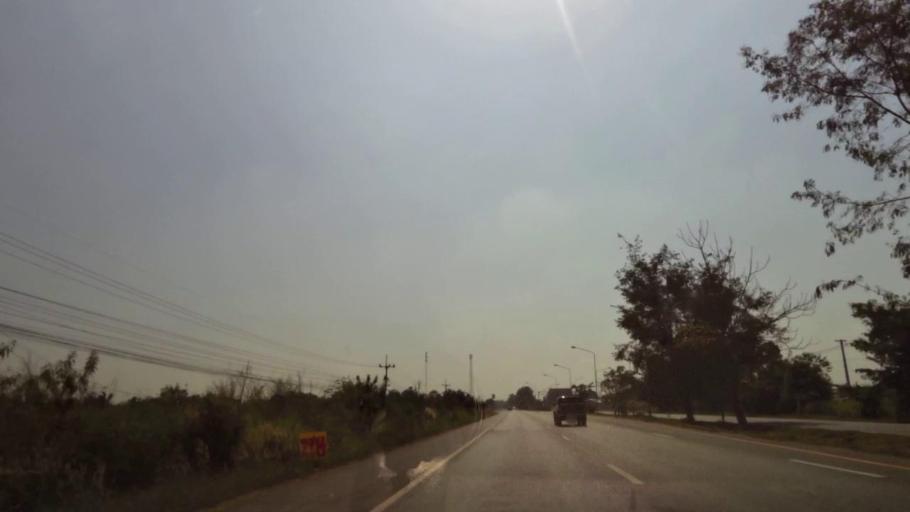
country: TH
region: Phichit
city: Wachira Barami
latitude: 16.3505
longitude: 100.1286
